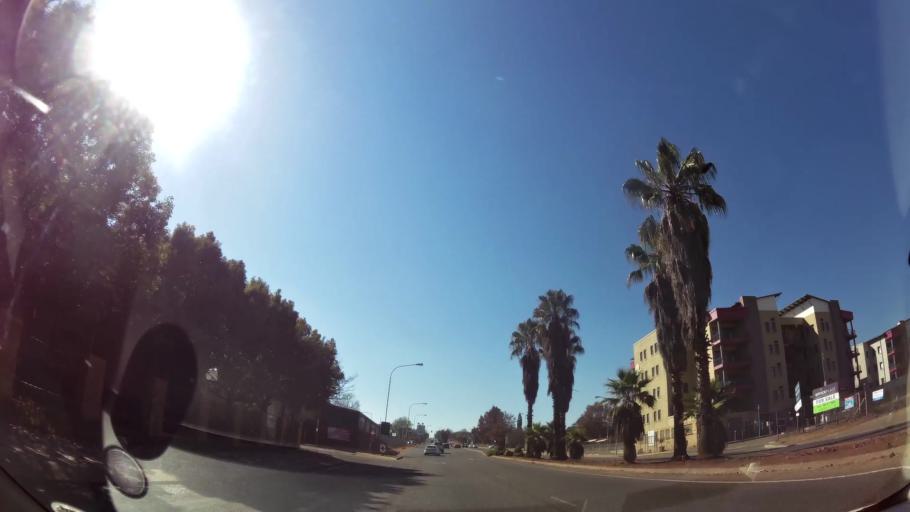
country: ZA
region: Gauteng
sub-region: City of Tshwane Metropolitan Municipality
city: Centurion
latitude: -25.8508
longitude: 28.1967
